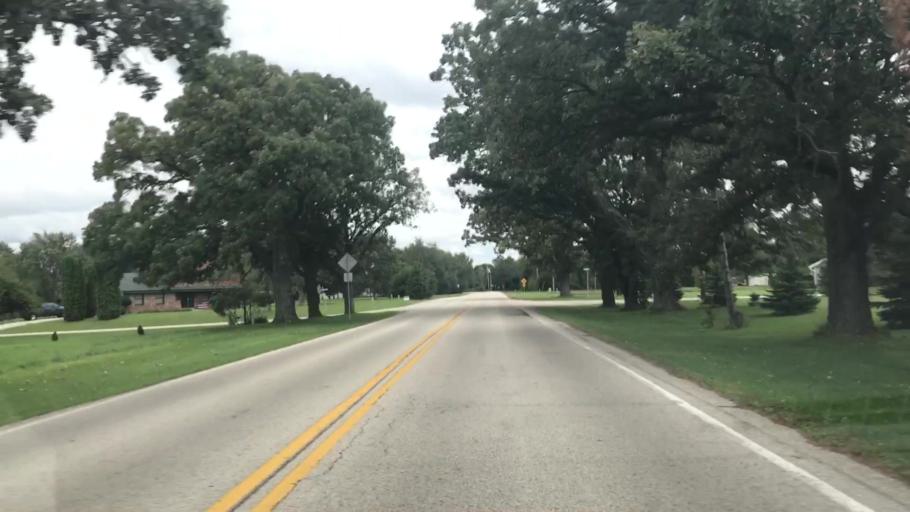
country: US
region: Wisconsin
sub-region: Waukesha County
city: North Prairie
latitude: 42.9039
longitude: -88.4051
